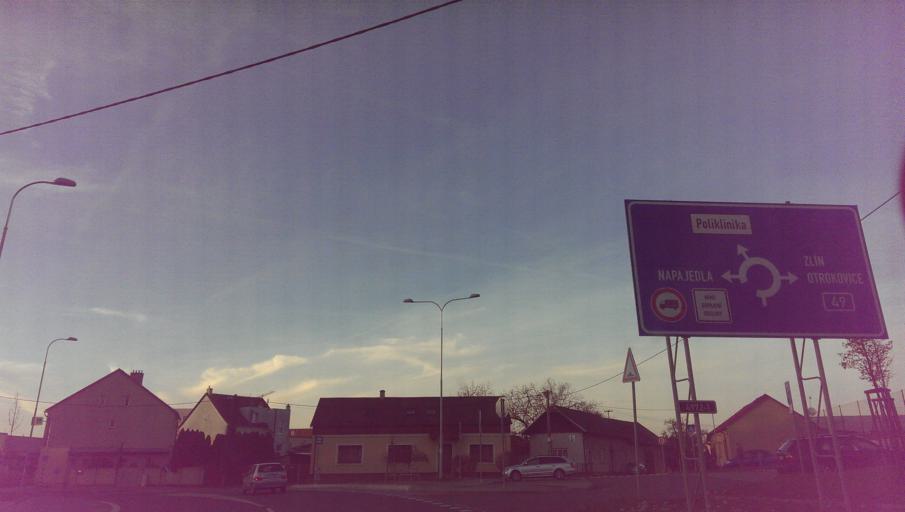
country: CZ
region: Zlin
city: Tecovice
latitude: 49.2069
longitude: 17.5966
